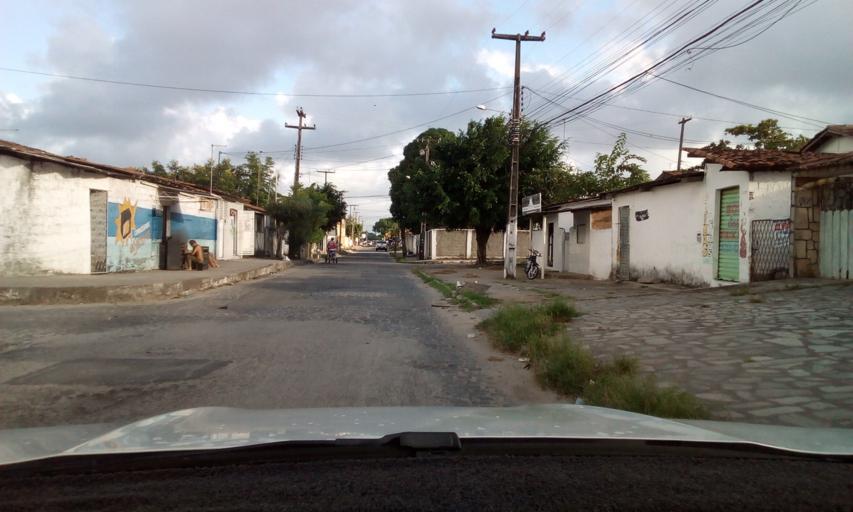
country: BR
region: Paraiba
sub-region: Joao Pessoa
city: Joao Pessoa
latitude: -7.1685
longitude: -34.8367
